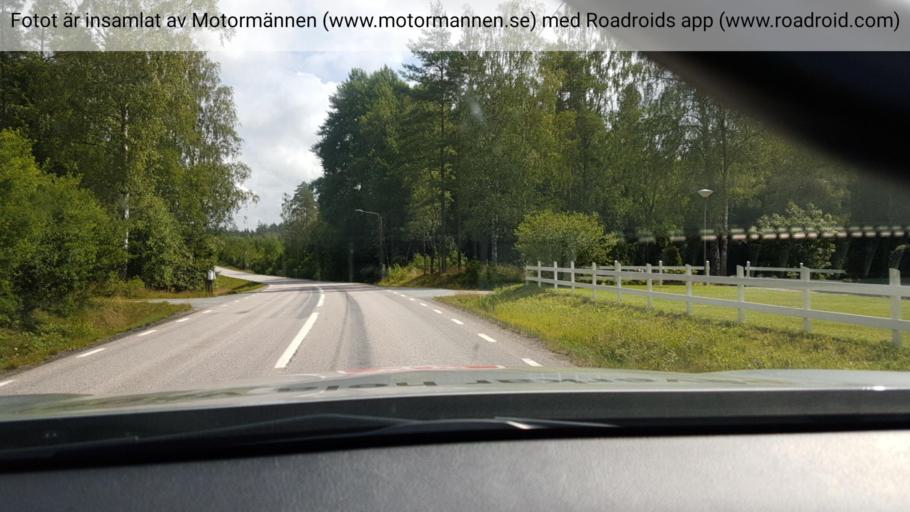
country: SE
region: Vaestra Goetaland
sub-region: Svenljunga Kommun
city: Svenljunga
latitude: 57.4887
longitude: 12.9625
